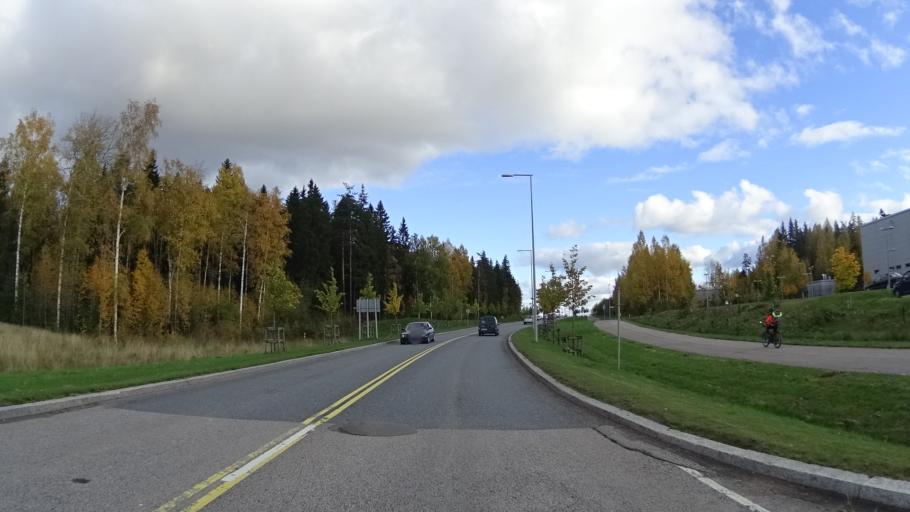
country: FI
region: Uusimaa
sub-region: Helsinki
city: Vantaa
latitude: 60.3028
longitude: 24.9422
